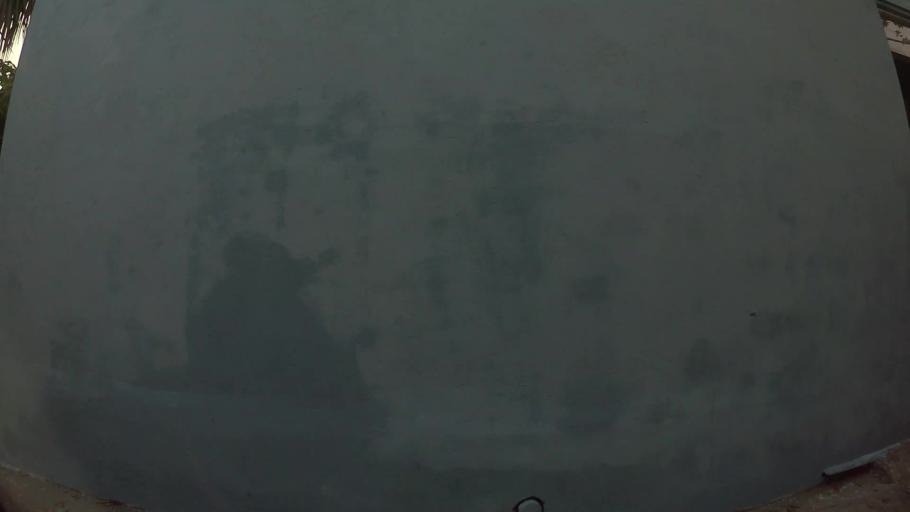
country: VN
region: Da Nang
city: Lien Chieu
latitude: 16.0490
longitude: 108.1581
